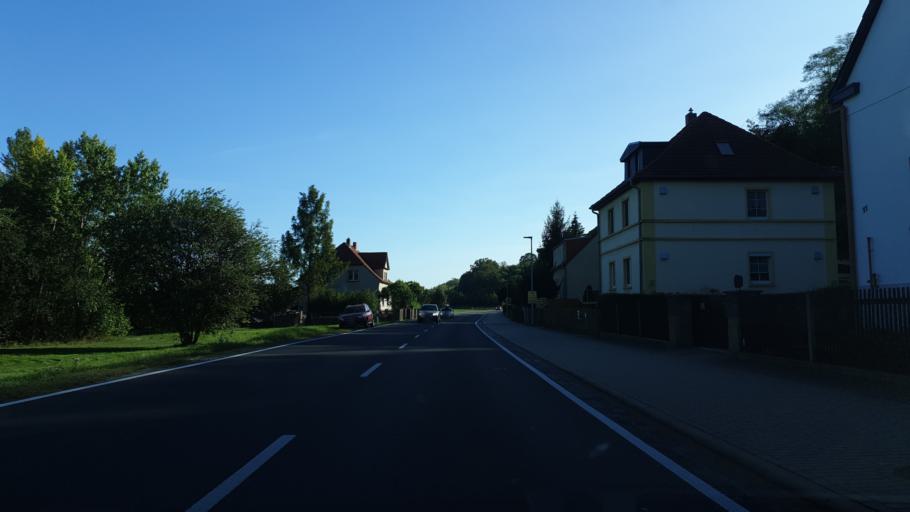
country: DE
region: Thuringia
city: Hartmannsdorf
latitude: 50.9607
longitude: 11.9850
